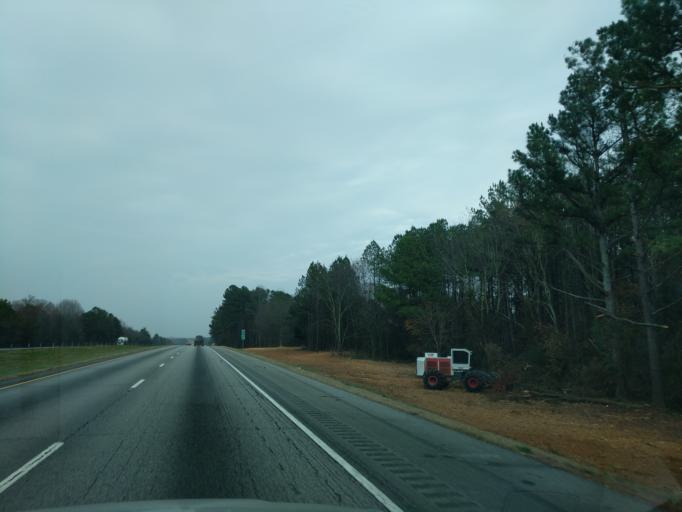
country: US
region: Georgia
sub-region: Franklin County
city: Carnesville
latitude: 34.3300
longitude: -83.3528
